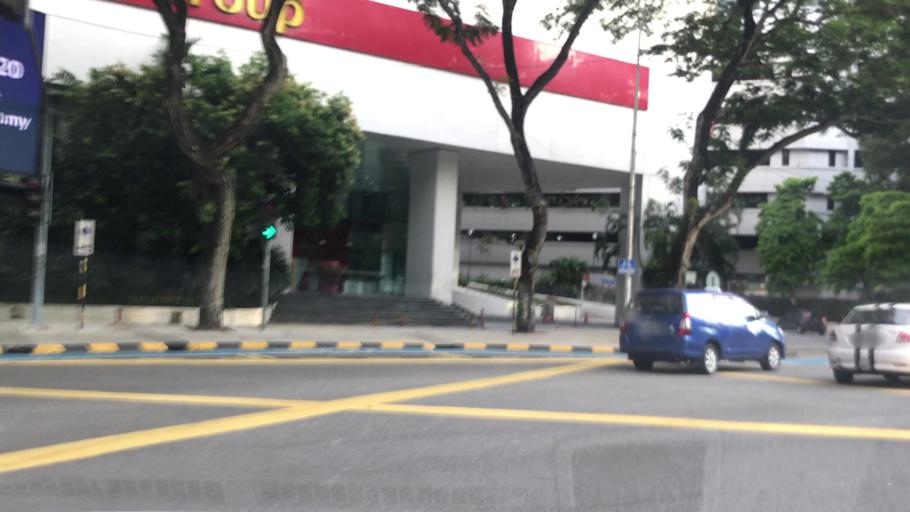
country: MY
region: Kuala Lumpur
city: Kuala Lumpur
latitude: 3.1508
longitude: 101.7064
